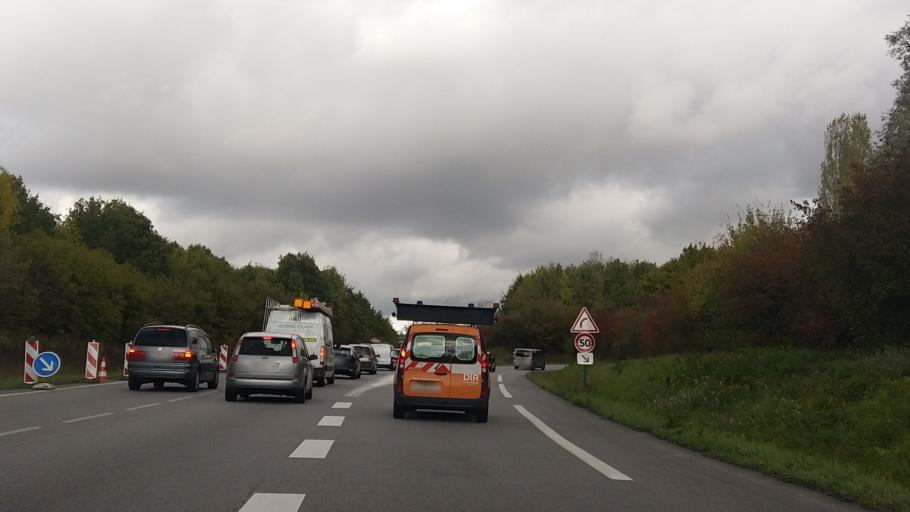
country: FR
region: Ile-de-France
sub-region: Departement du Val-d'Oise
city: Mours
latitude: 49.1256
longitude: 2.2540
